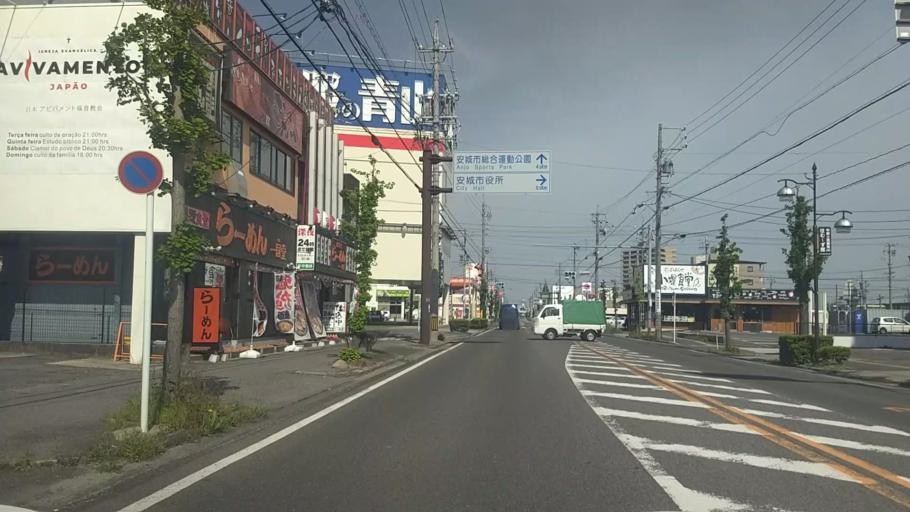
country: JP
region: Aichi
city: Anjo
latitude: 34.9536
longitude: 137.0798
